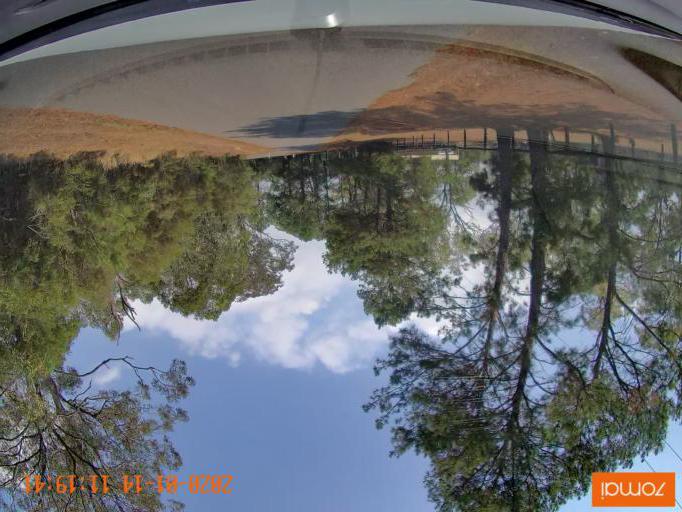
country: AU
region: New South Wales
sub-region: Lake Macquarie Shire
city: Cooranbong
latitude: -33.0991
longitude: 151.4601
